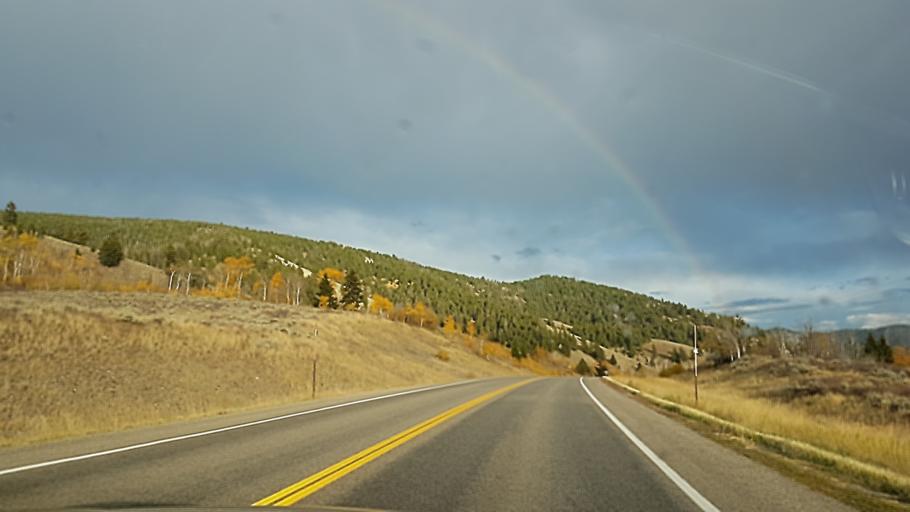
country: US
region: Montana
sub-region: Gallatin County
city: West Yellowstone
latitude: 44.6629
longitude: -111.3673
